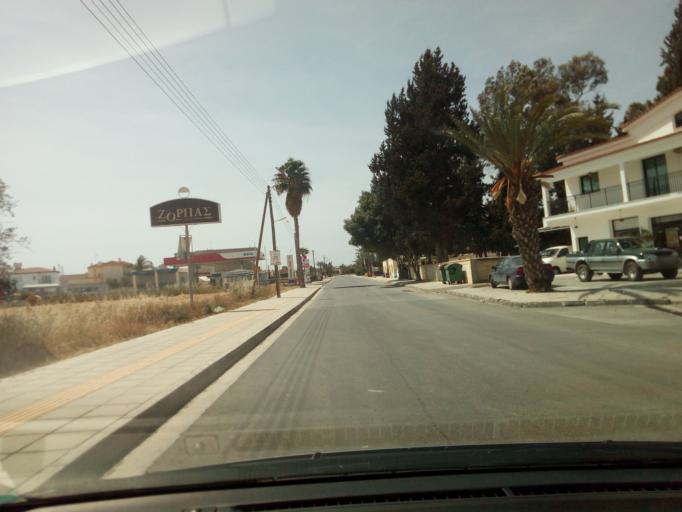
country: CY
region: Larnaka
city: Athienou
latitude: 35.0587
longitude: 33.5365
